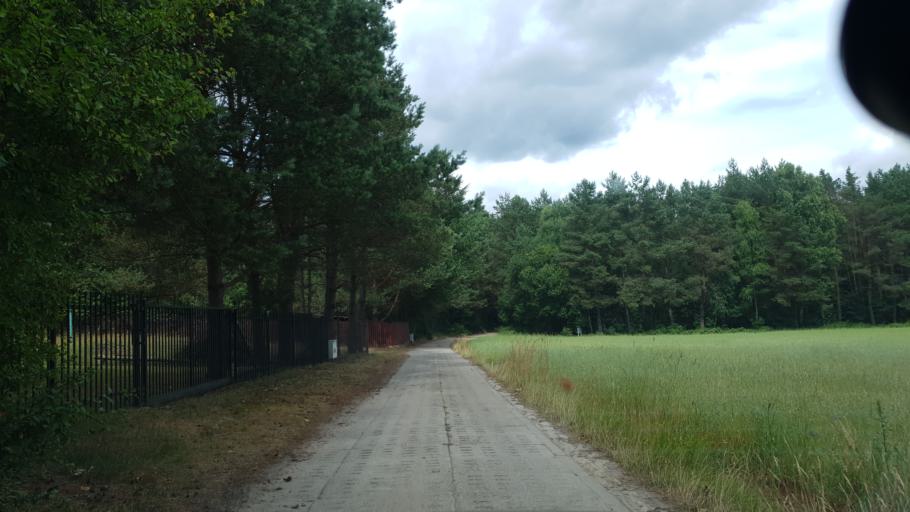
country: PL
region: Pomeranian Voivodeship
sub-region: Powiat kartuski
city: Stezyca
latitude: 54.2481
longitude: 17.9943
